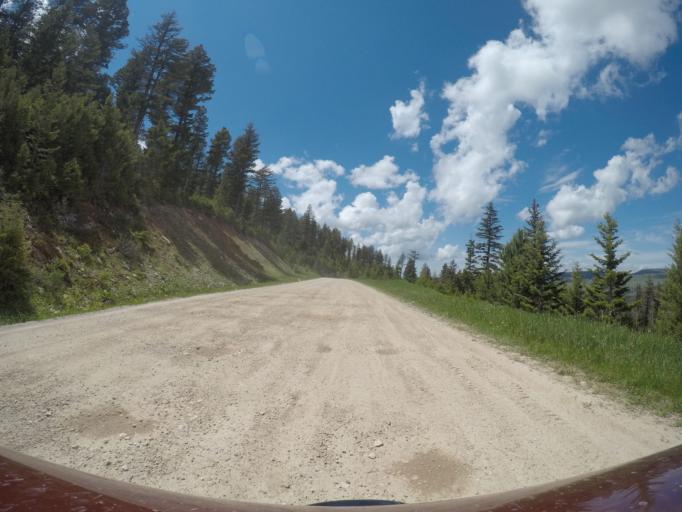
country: US
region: Wyoming
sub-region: Big Horn County
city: Lovell
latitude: 45.1955
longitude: -108.4898
